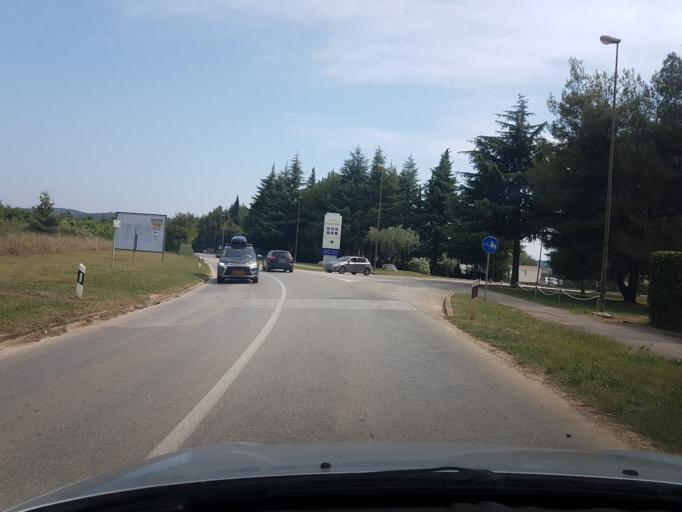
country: HR
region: Istarska
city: Vrsar
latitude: 45.1657
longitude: 13.6094
